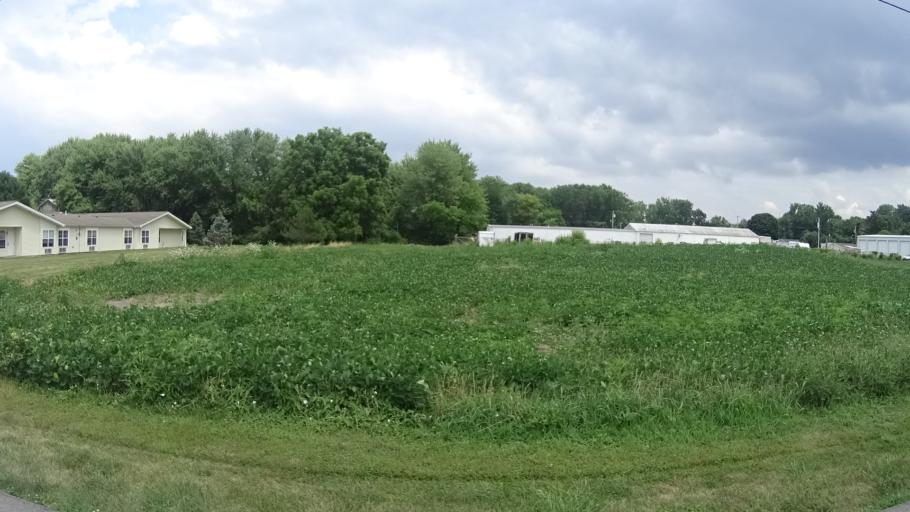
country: US
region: Ohio
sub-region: Erie County
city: Sandusky
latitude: 41.4405
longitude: -82.7540
